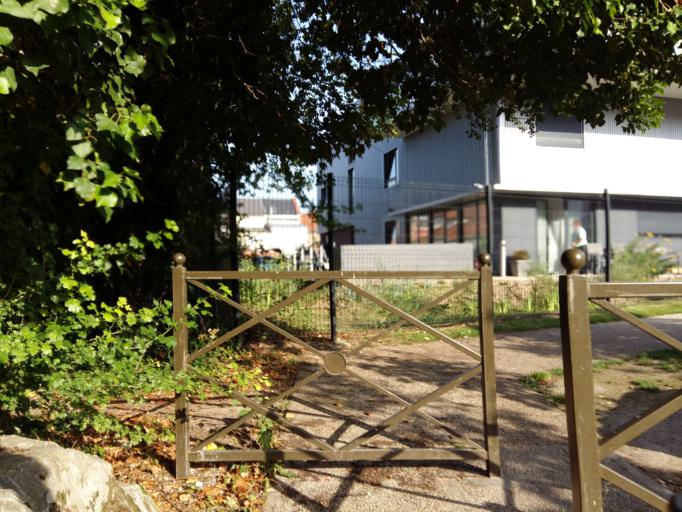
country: FR
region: Picardie
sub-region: Departement de la Somme
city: Amiens
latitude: 49.9018
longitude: 2.2892
